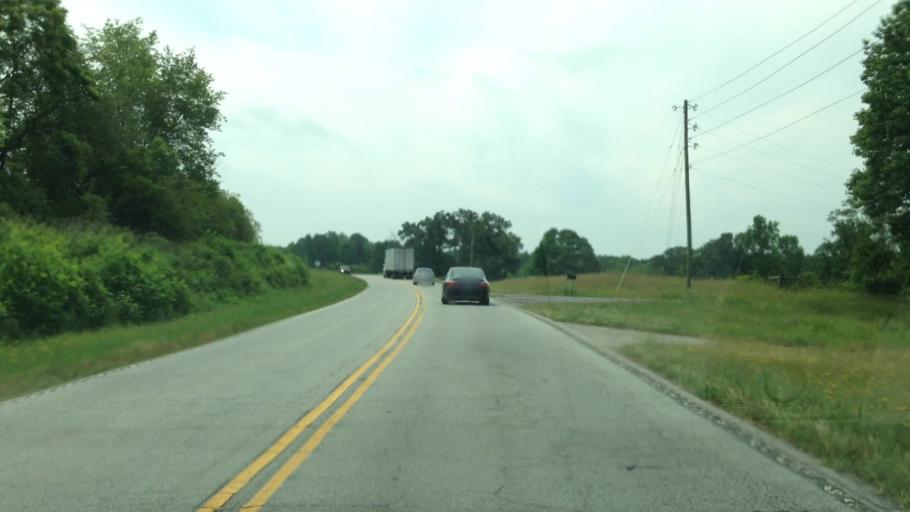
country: US
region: South Carolina
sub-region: Oconee County
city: Westminster
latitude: 34.6492
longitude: -83.0492
